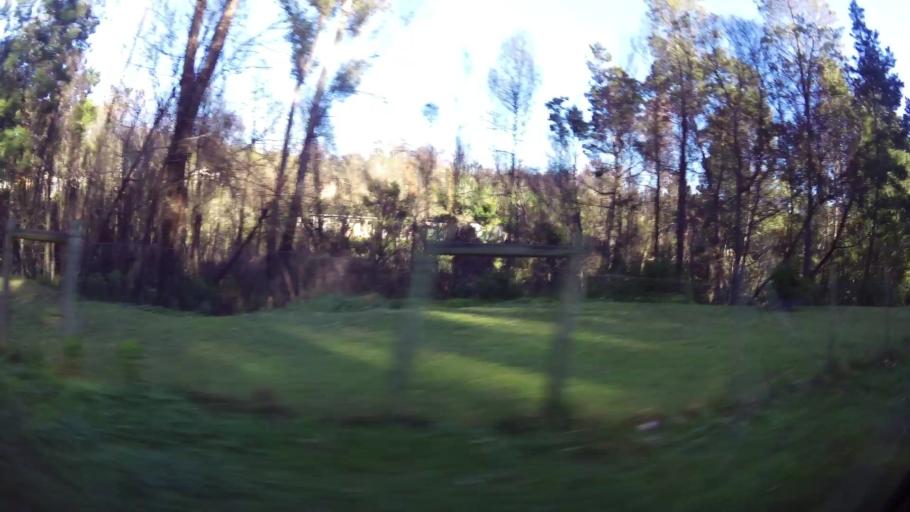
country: ZA
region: Western Cape
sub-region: Eden District Municipality
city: Knysna
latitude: -34.0325
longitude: 23.0148
